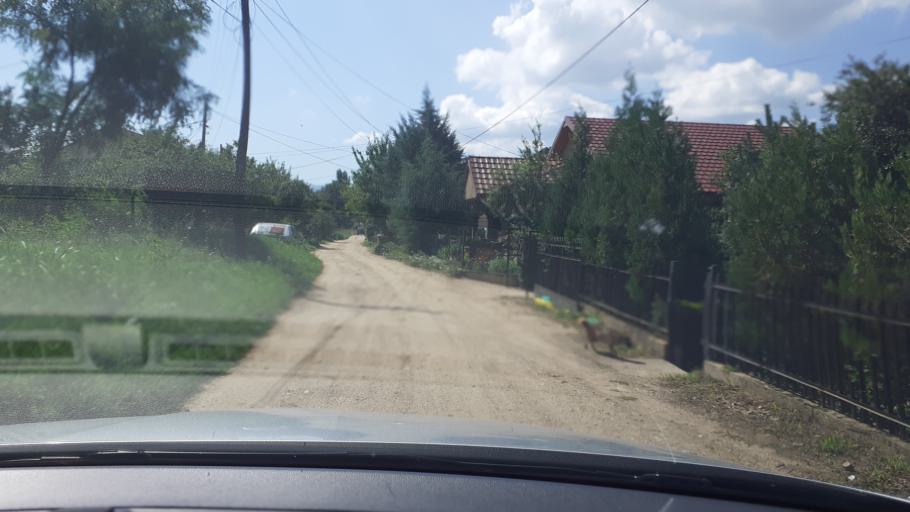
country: MK
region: Vasilevo
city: Vasilevo
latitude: 41.4709
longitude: 22.6420
